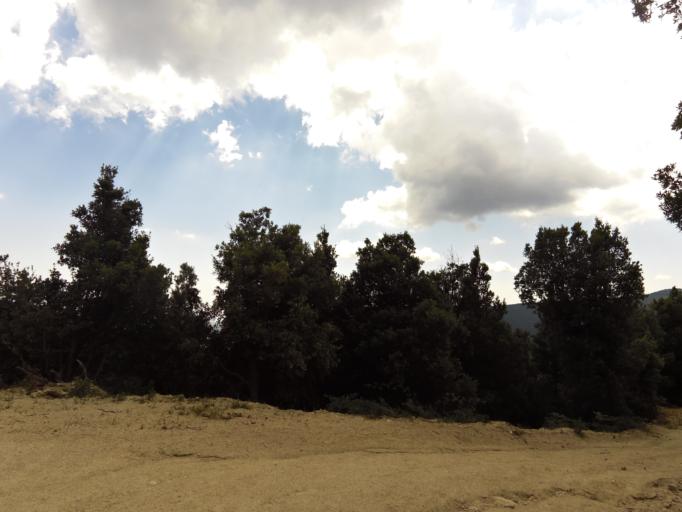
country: IT
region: Calabria
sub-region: Provincia di Reggio Calabria
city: Bivongi
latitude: 38.5088
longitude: 16.3968
